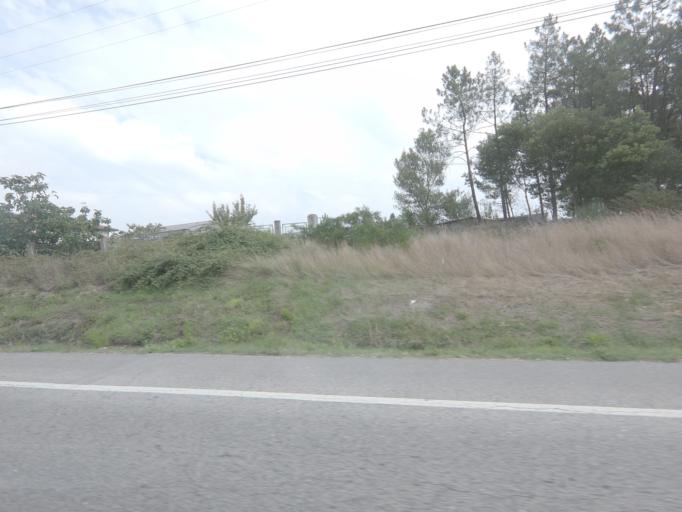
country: PT
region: Leiria
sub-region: Leiria
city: Leiria
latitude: 39.7726
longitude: -8.7663
